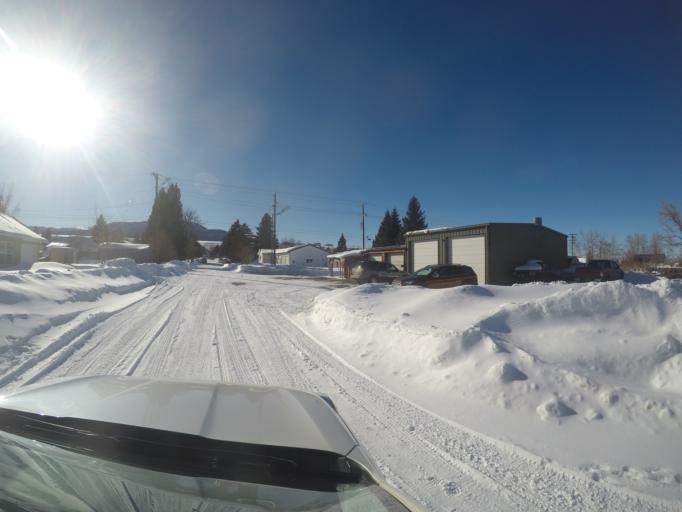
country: US
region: Montana
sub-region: Carbon County
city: Red Lodge
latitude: 45.1910
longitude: -109.2433
